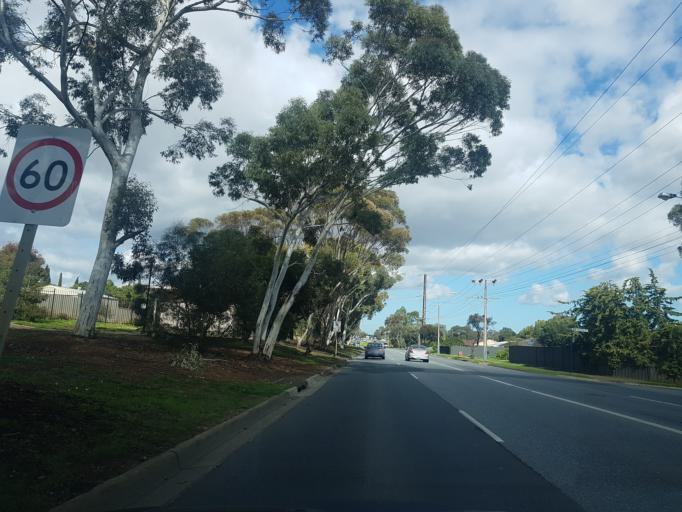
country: AU
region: South Australia
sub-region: Salisbury
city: Salisbury
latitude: -34.7947
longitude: 138.6600
